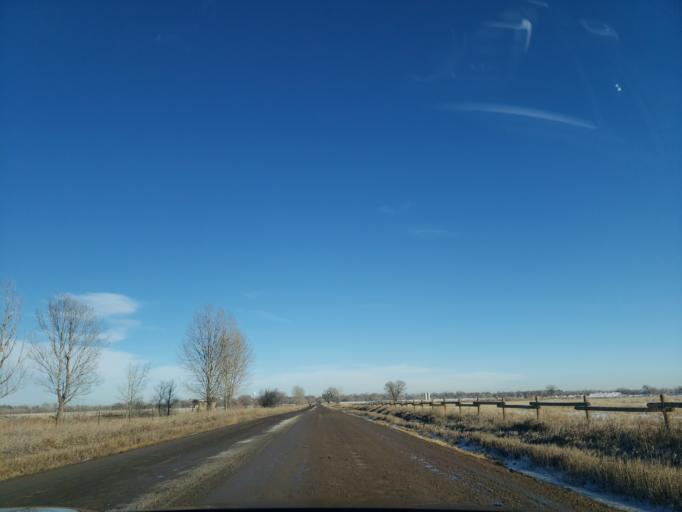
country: US
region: Colorado
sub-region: Larimer County
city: Fort Collins
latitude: 40.5377
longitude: -105.0139
